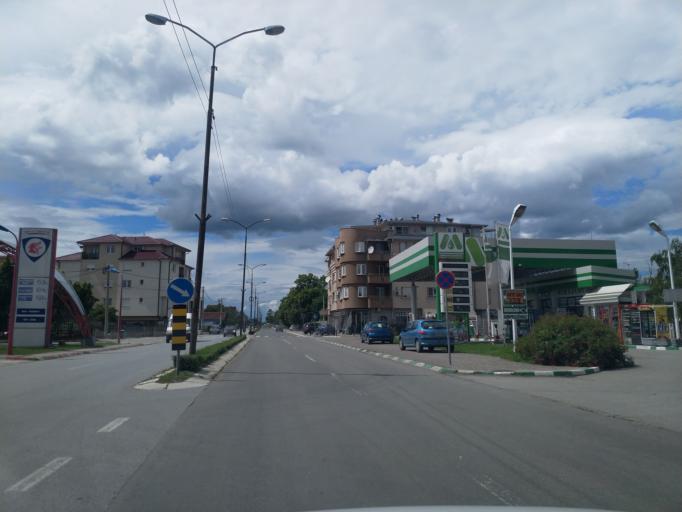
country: RS
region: Central Serbia
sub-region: Pomoravski Okrug
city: Paracin
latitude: 43.8669
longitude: 21.4061
